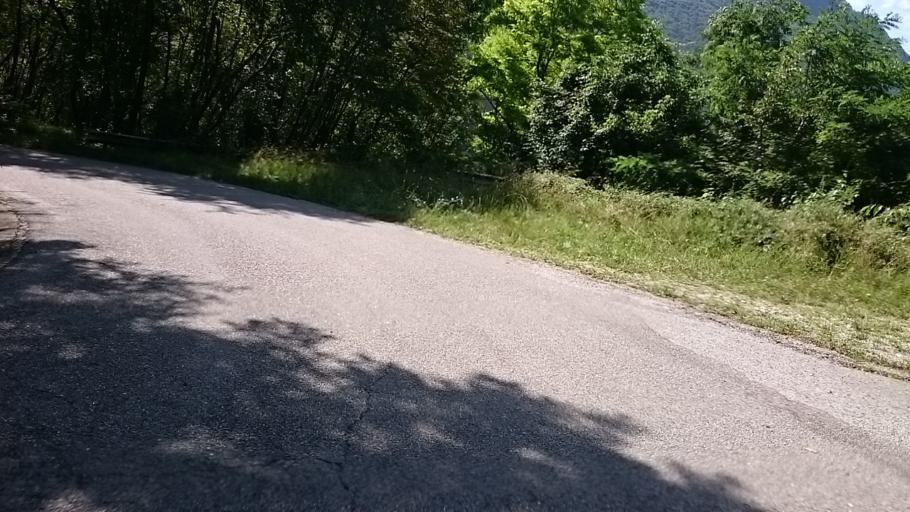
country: IT
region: Veneto
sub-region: Provincia di Belluno
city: Farra d'Alpago
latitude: 46.0723
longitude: 12.3349
